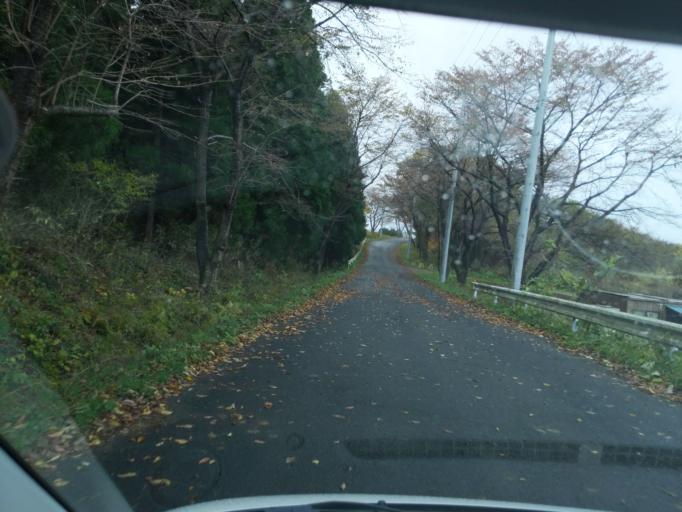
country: JP
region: Iwate
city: Mizusawa
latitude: 39.0650
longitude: 141.0459
